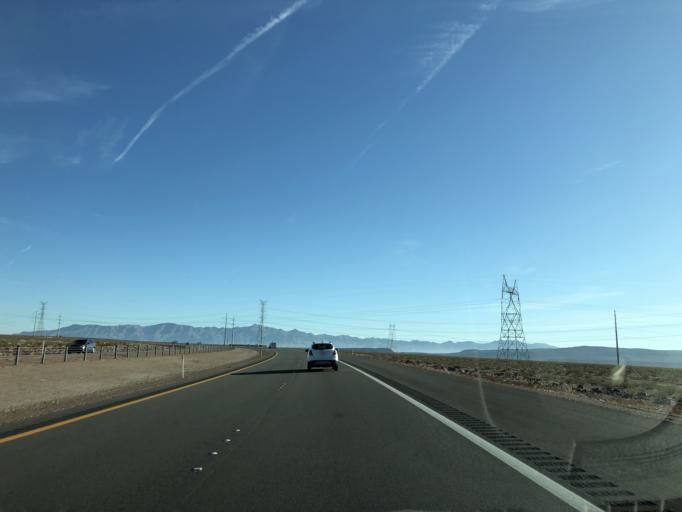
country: US
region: Nevada
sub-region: Clark County
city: Boulder City
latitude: 35.9393
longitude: -114.8176
